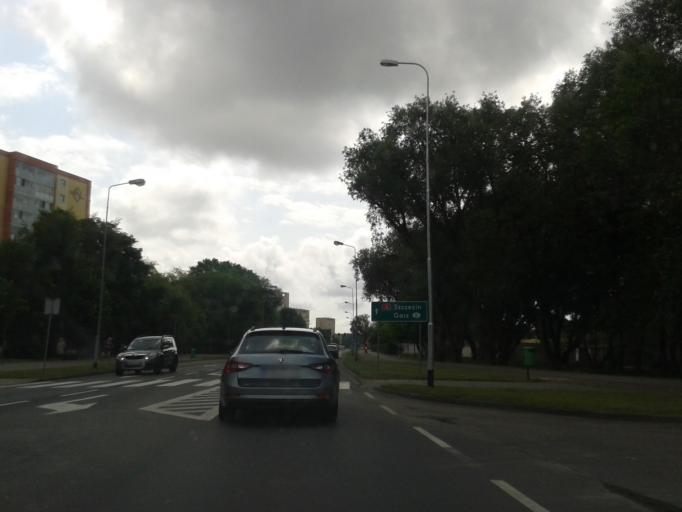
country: PL
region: West Pomeranian Voivodeship
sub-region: Swinoujscie
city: Swinoujscie
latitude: 53.9102
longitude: 14.2320
